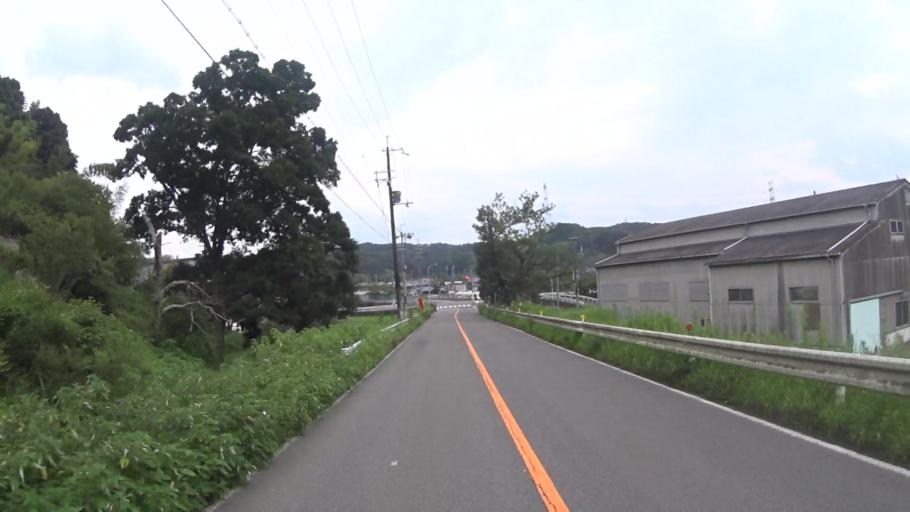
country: JP
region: Kyoto
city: Tanabe
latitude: 34.7849
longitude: 135.7510
